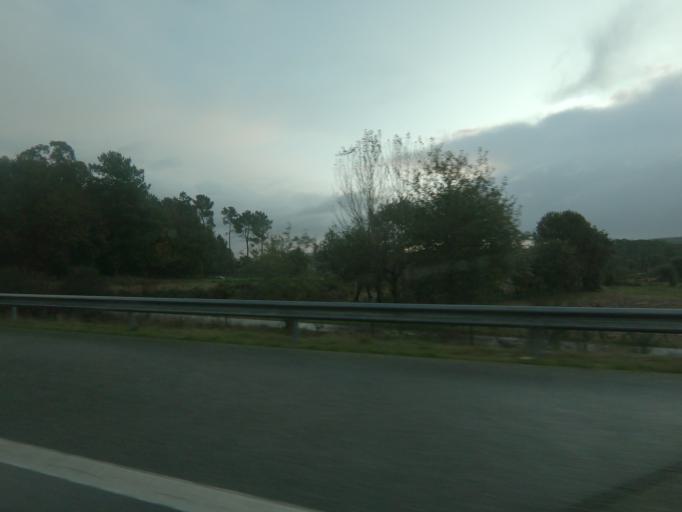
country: PT
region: Braga
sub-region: Vila Verde
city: Prado
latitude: 41.6608
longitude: -8.5482
